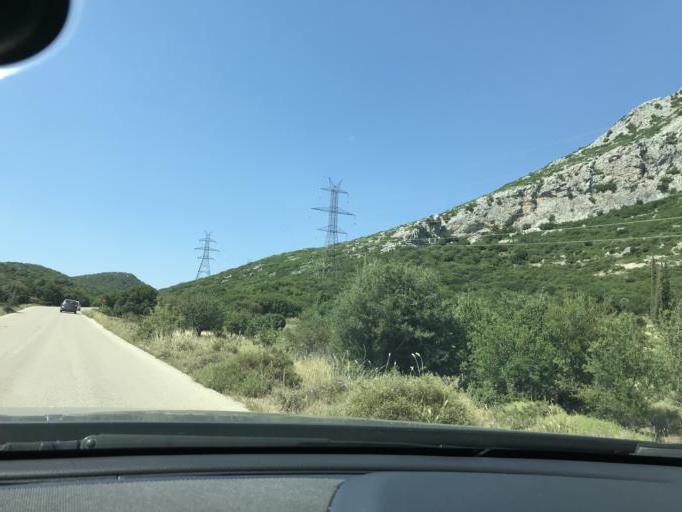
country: GR
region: Central Greece
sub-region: Nomos Voiotias
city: Distomo
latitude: 38.5024
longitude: 22.7030
